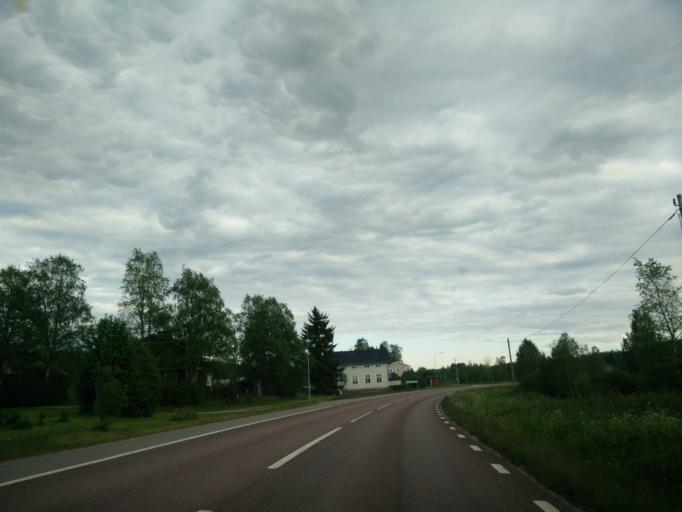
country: SE
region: Jaemtland
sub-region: Harjedalens Kommun
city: Sveg
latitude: 62.2794
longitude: 14.8059
